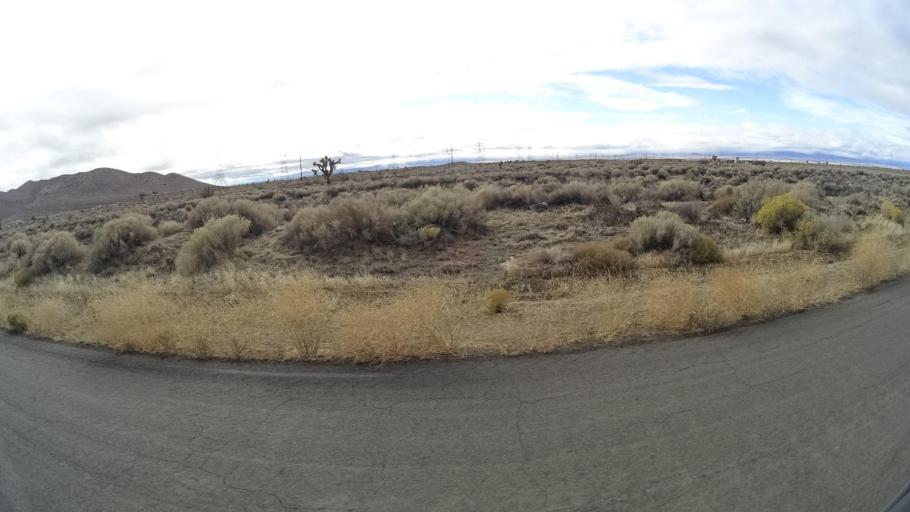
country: US
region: California
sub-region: Kern County
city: Rosamond
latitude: 34.8927
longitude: -118.3005
